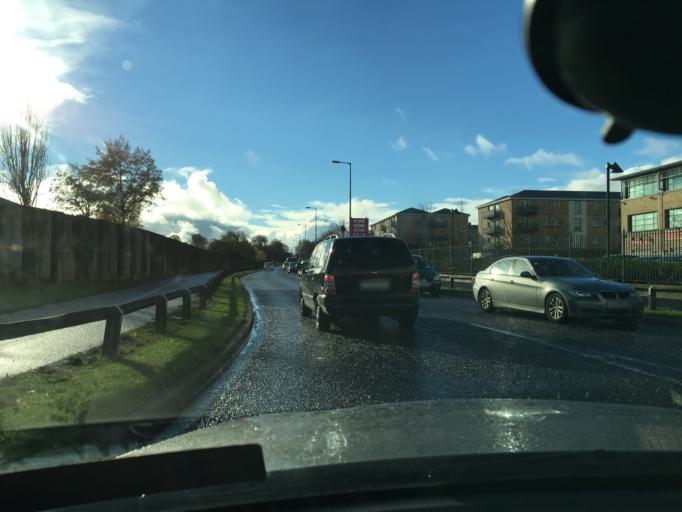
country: IE
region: Leinster
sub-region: Fingal County
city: Blanchardstown
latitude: 53.3889
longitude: -6.3883
